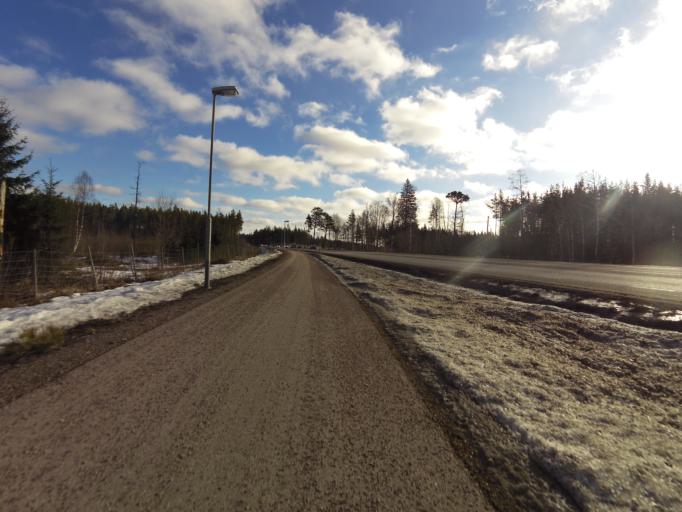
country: SE
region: Gaevleborg
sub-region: Gavle Kommun
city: Gavle
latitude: 60.6456
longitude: 17.2633
